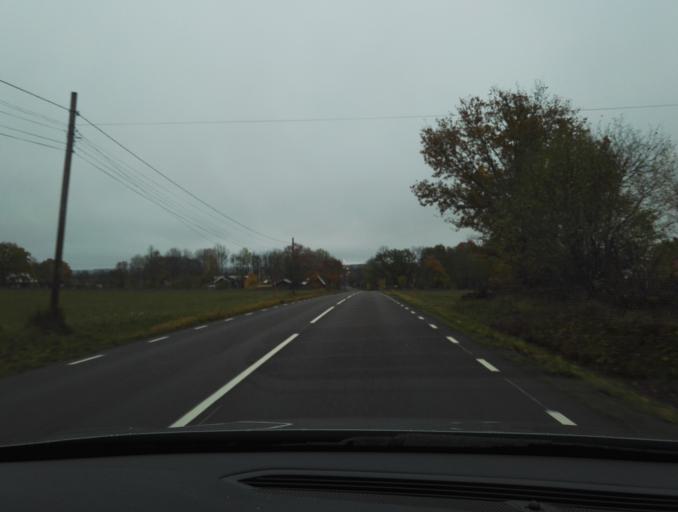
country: SE
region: Kronoberg
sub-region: Vaxjo Kommun
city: Rottne
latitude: 57.0240
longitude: 14.8424
